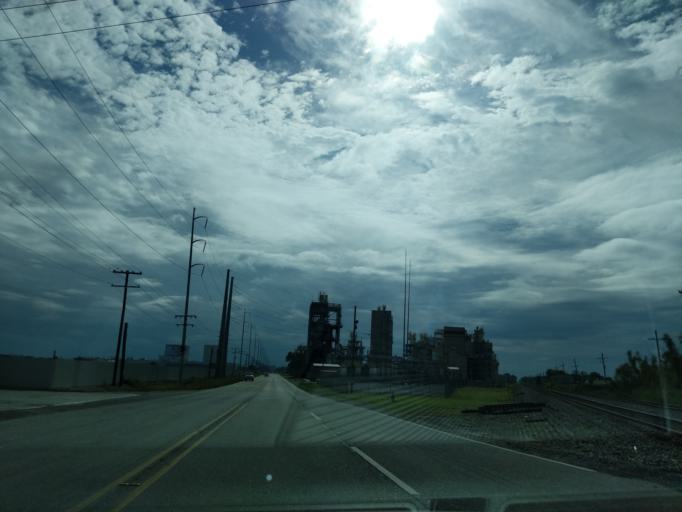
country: US
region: Louisiana
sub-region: Saint Bernard Parish
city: Chalmette
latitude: 30.0368
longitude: -89.9063
